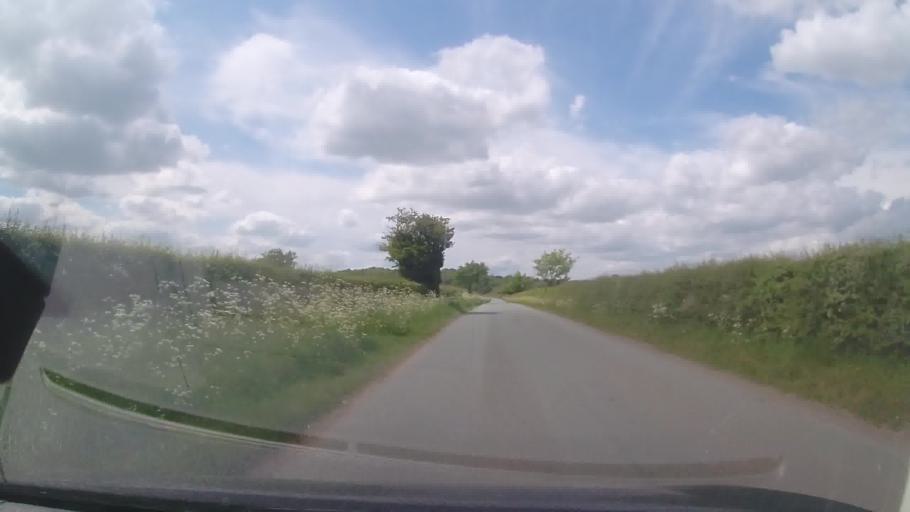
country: GB
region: England
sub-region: Shropshire
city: Shawbury
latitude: 52.8071
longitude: -2.6624
